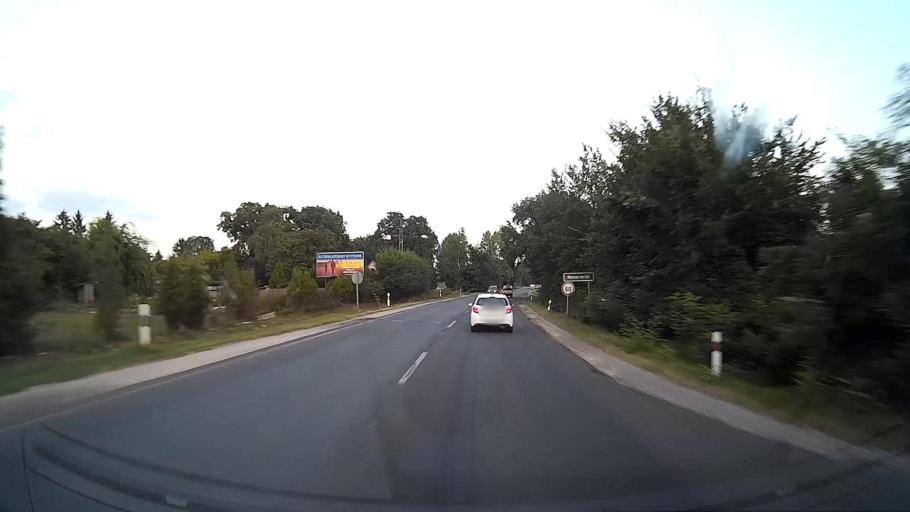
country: HU
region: Pest
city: Nyaregyhaza
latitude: 47.3148
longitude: 19.4926
